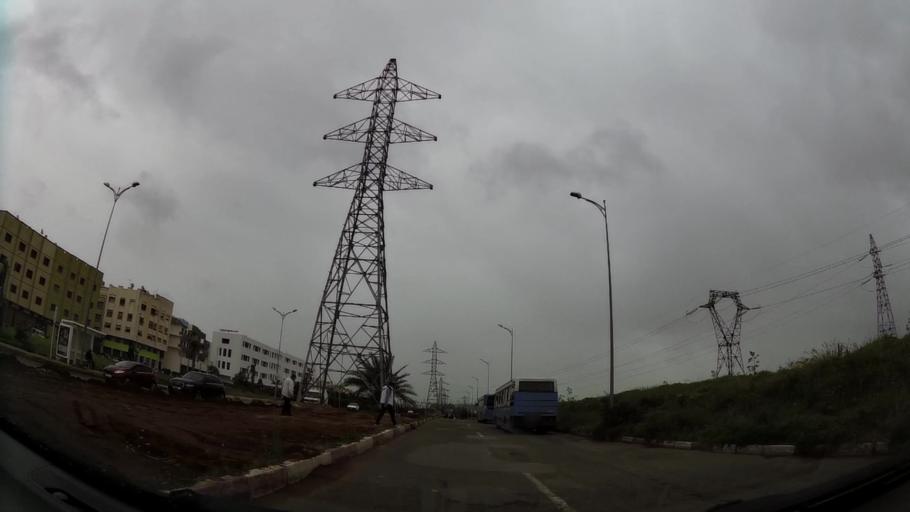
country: MA
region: Grand Casablanca
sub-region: Casablanca
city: Casablanca
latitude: 33.5302
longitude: -7.6173
